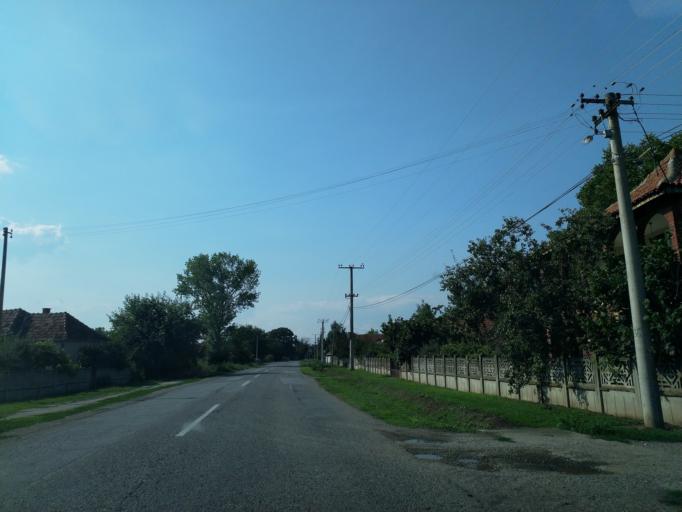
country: RS
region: Central Serbia
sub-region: Rasinski Okrug
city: Cicevac
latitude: 43.7552
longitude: 21.4360
